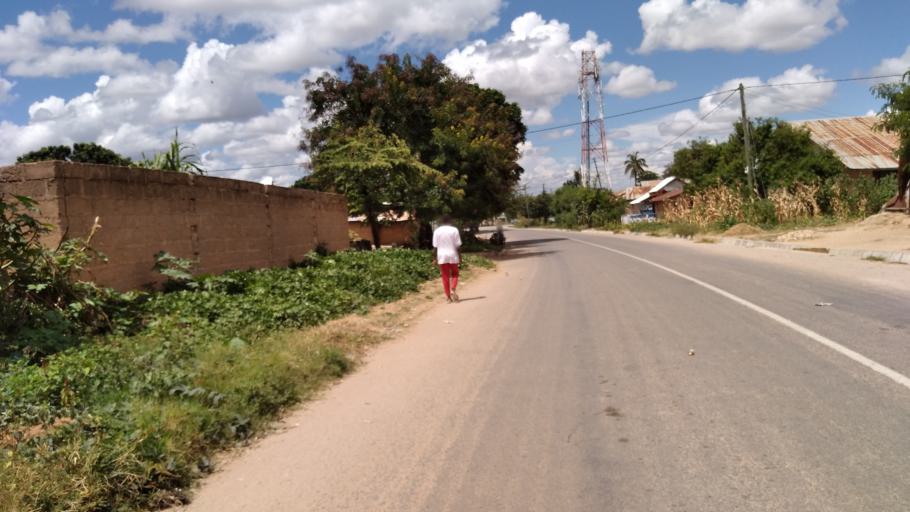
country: TZ
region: Dodoma
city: Dodoma
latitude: -6.1600
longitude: 35.7377
